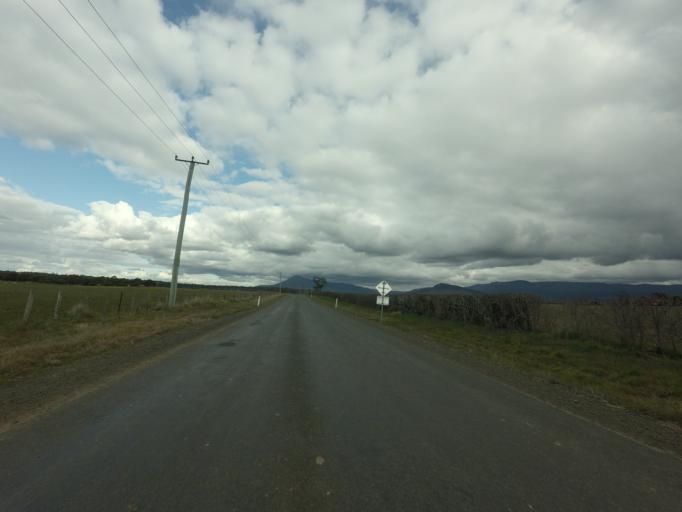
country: AU
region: Tasmania
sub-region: Northern Midlands
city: Longford
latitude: -41.7887
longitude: 147.1122
